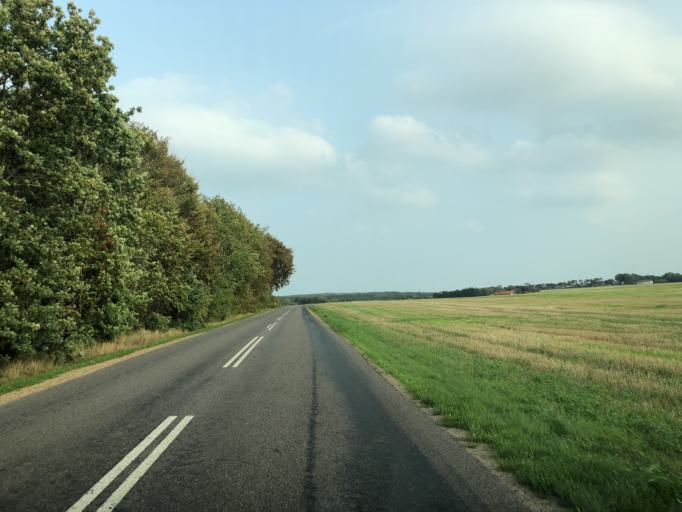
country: DK
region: Central Jutland
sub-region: Ringkobing-Skjern Kommune
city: Videbaek
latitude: 56.0516
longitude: 8.6985
